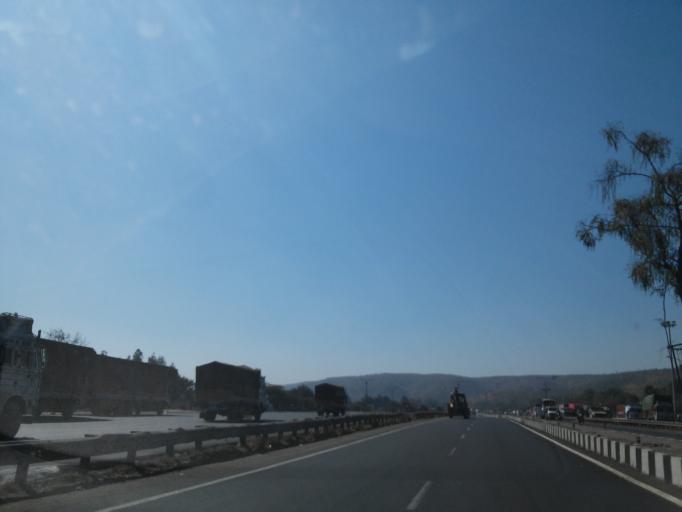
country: IN
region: Gujarat
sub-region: Sabar Kantha
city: Meghraj
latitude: 23.7209
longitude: 73.3976
